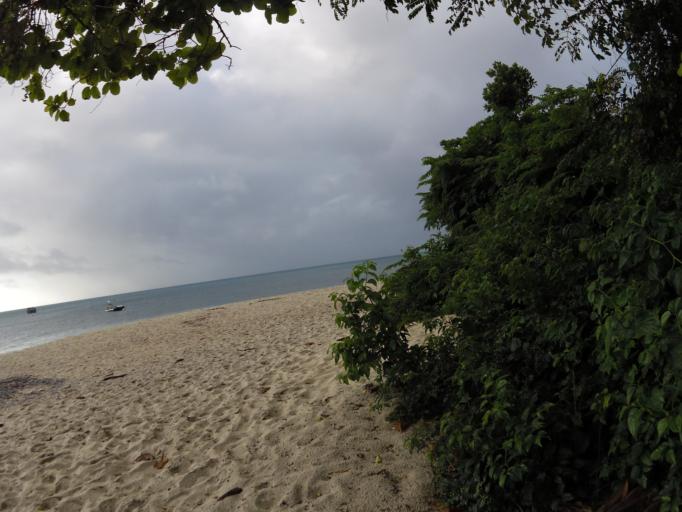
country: AU
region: Queensland
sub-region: Cairns
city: Yorkeys Knob
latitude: -16.7579
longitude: 145.9724
